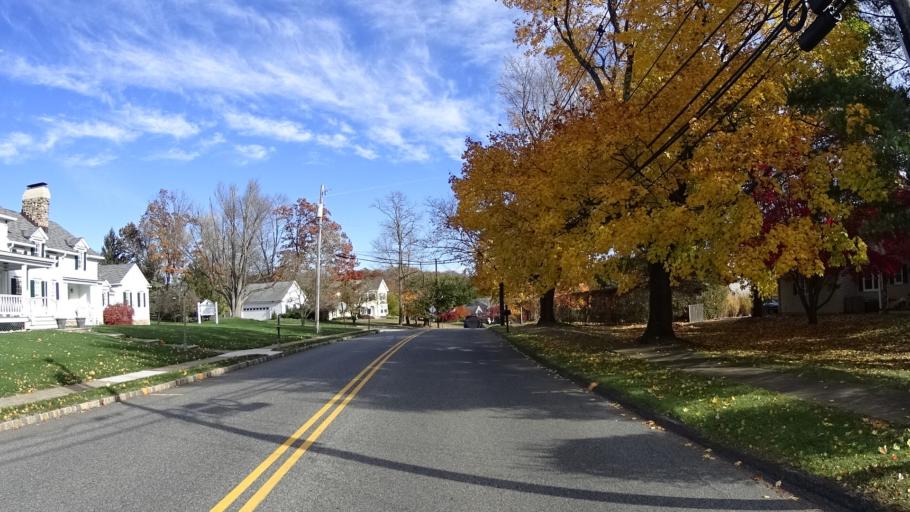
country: US
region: New Jersey
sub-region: Morris County
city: Mendham
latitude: 40.7810
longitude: -74.5879
